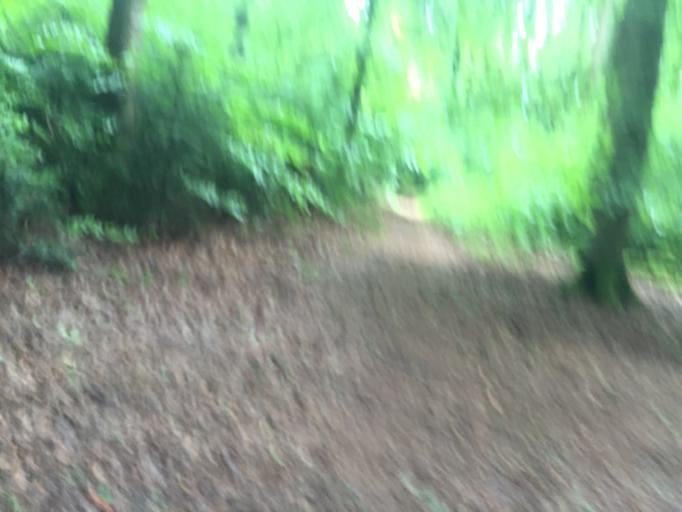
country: CH
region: Bern
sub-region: Bern-Mittelland District
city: Koniz
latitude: 46.9271
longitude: 7.4015
